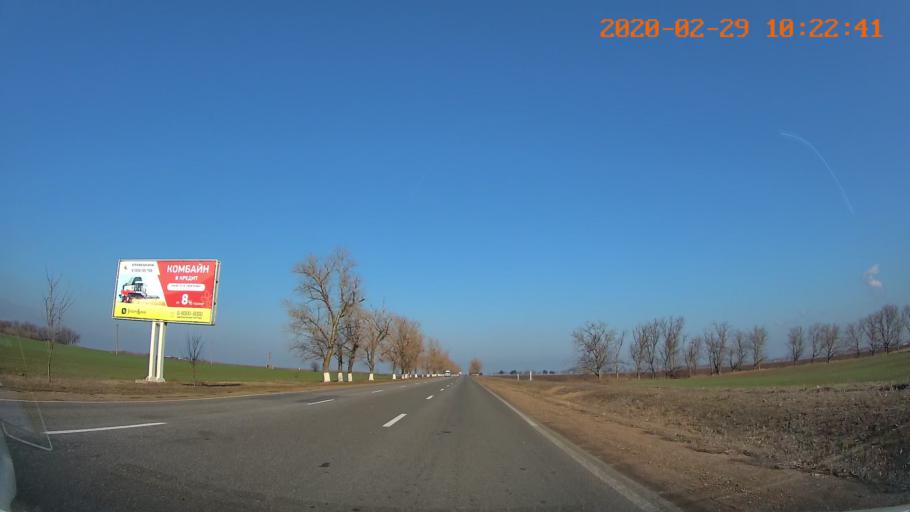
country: MD
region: Telenesti
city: Tiraspolul Nou
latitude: 46.8782
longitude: 29.6058
